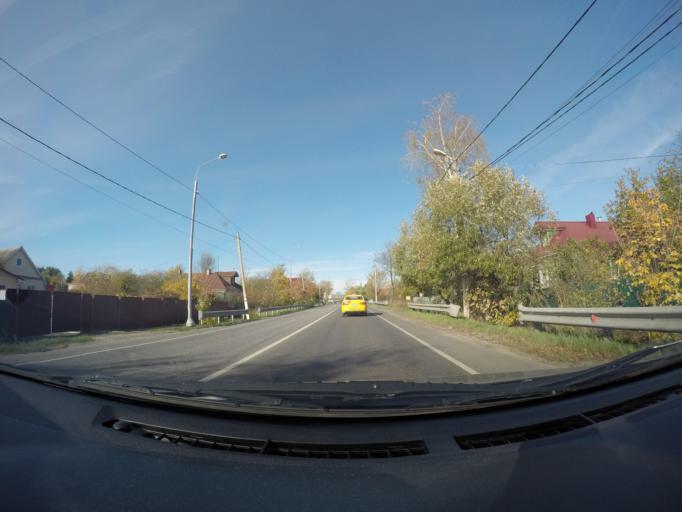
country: RU
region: Moskovskaya
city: Gzhel'
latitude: 55.6251
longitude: 38.3713
